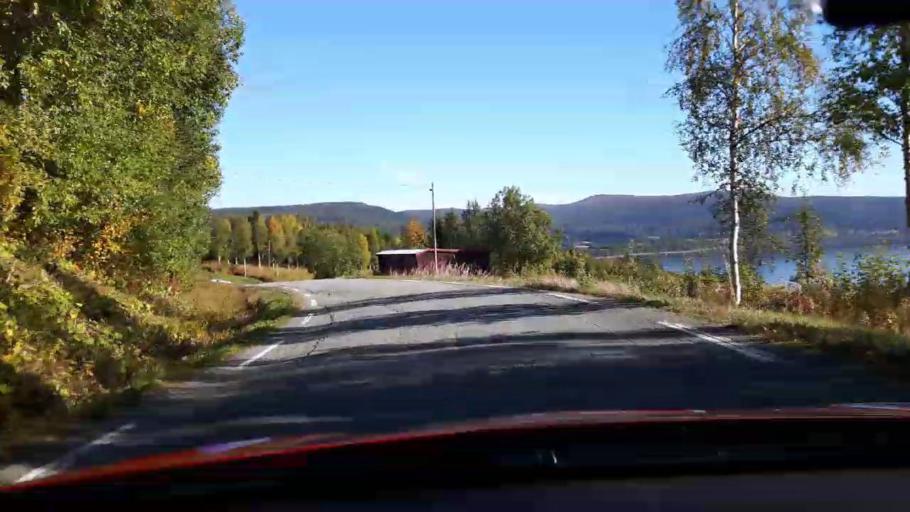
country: NO
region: Nord-Trondelag
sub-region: Lierne
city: Sandvika
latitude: 64.6315
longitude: 13.6908
